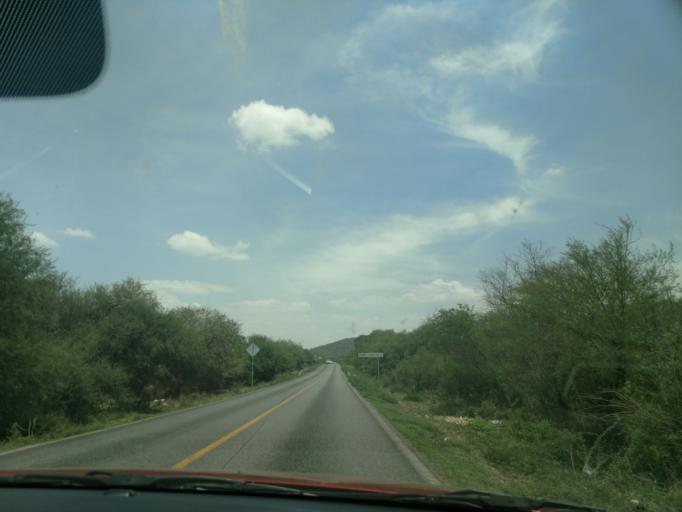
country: MX
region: San Luis Potosi
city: Ciudad Fernandez
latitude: 22.0039
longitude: -100.1457
